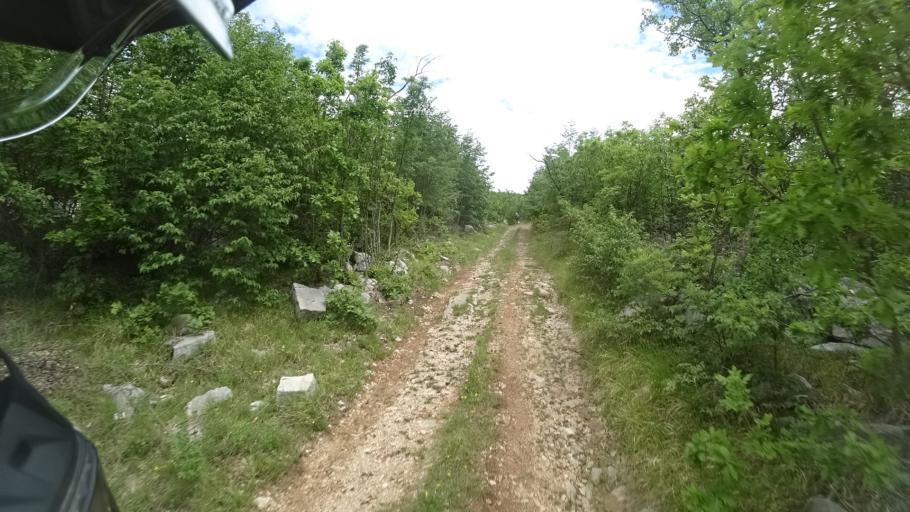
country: HR
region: Splitsko-Dalmatinska
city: Hrvace
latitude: 43.8844
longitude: 16.5853
